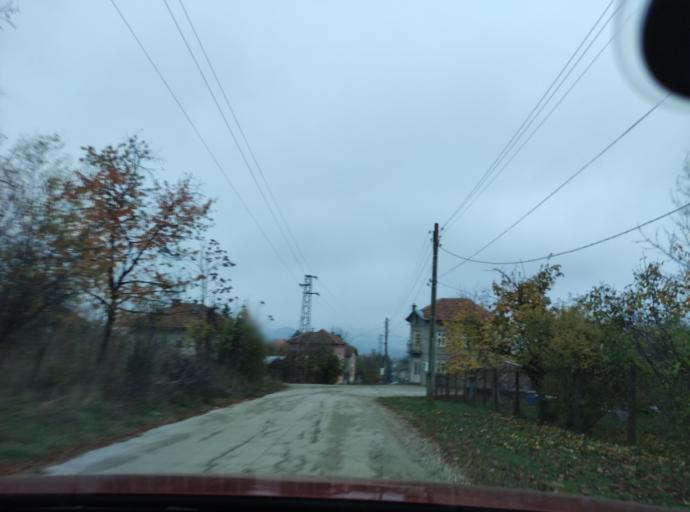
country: BG
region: Lovech
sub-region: Obshtina Yablanitsa
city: Yablanitsa
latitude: 43.0965
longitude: 24.0758
